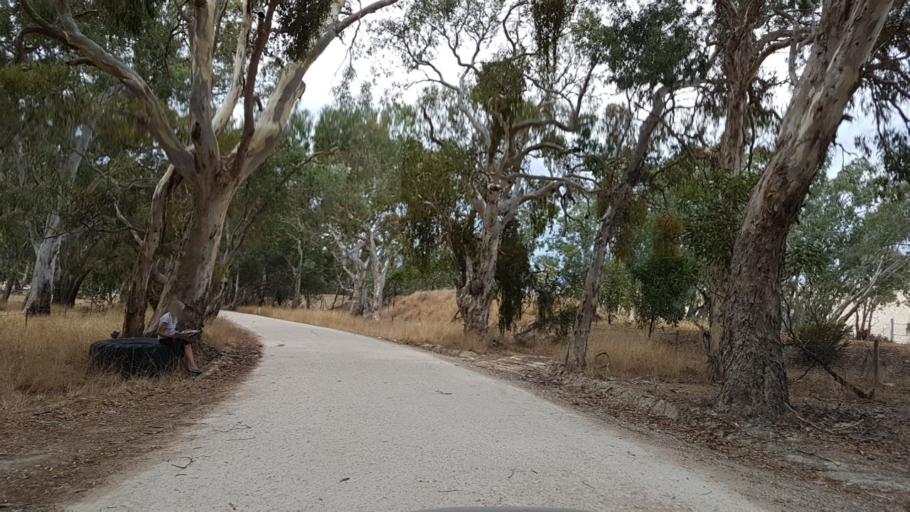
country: AU
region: South Australia
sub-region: Adelaide Hills
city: Birdwood
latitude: -34.7916
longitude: 138.9701
